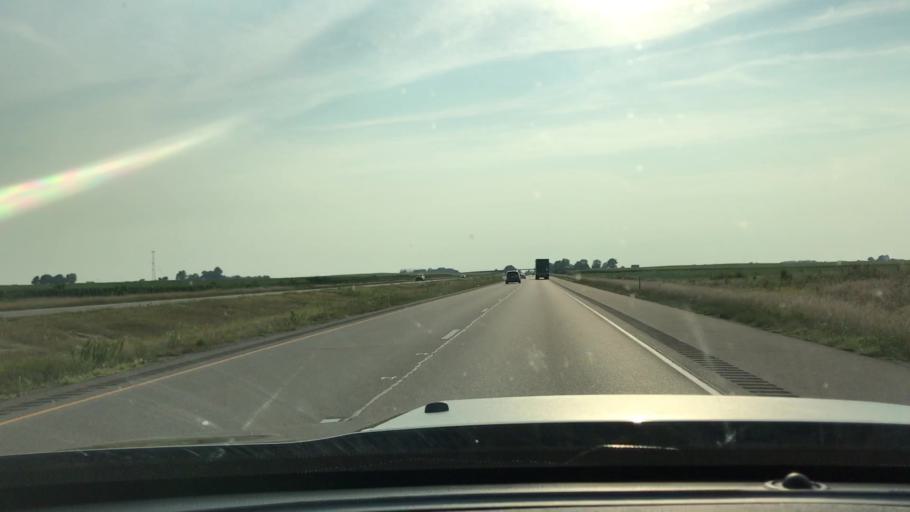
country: US
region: Illinois
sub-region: Bureau County
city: Princeton
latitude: 41.3946
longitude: -89.6087
